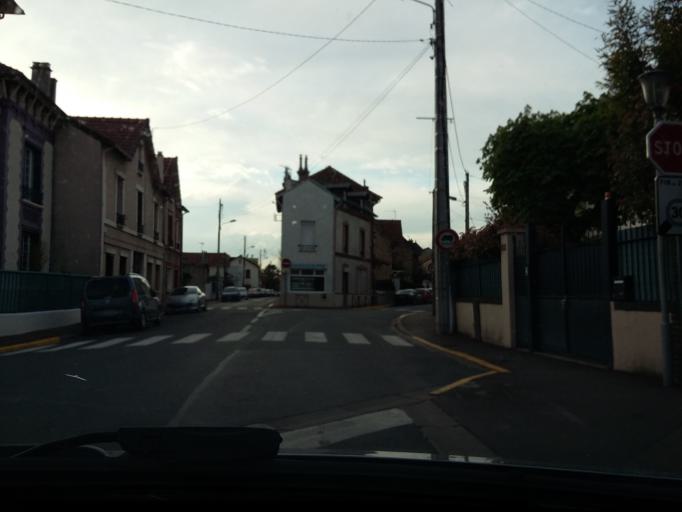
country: FR
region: Ile-de-France
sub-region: Departement du Val-d'Oise
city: Ermont
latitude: 48.9828
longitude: 2.2690
